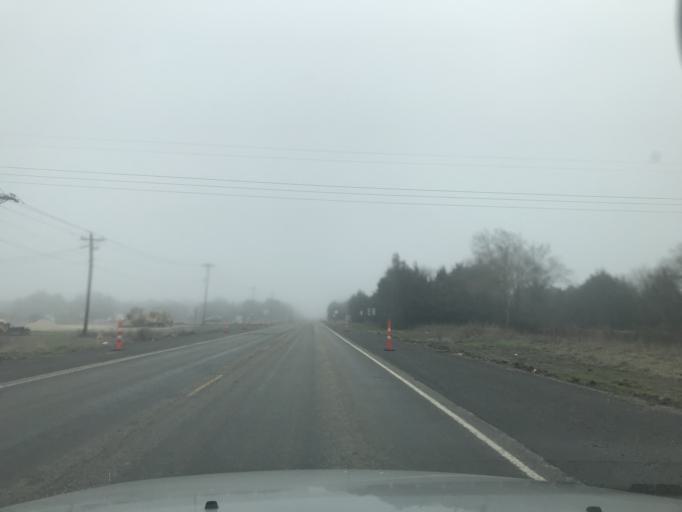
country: US
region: Texas
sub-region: Hunt County
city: Caddo Mills
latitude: 33.0567
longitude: -96.2370
